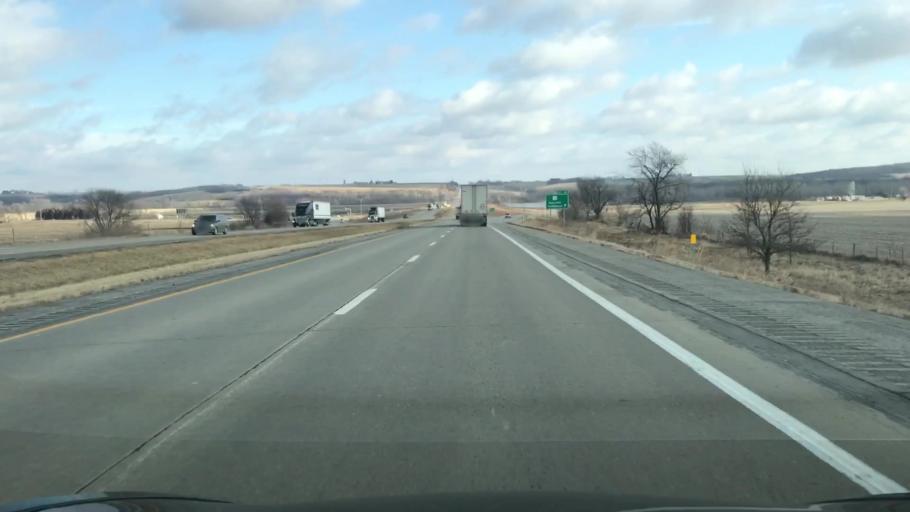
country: US
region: Iowa
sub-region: Cass County
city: Atlantic
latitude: 41.4971
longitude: -94.9502
